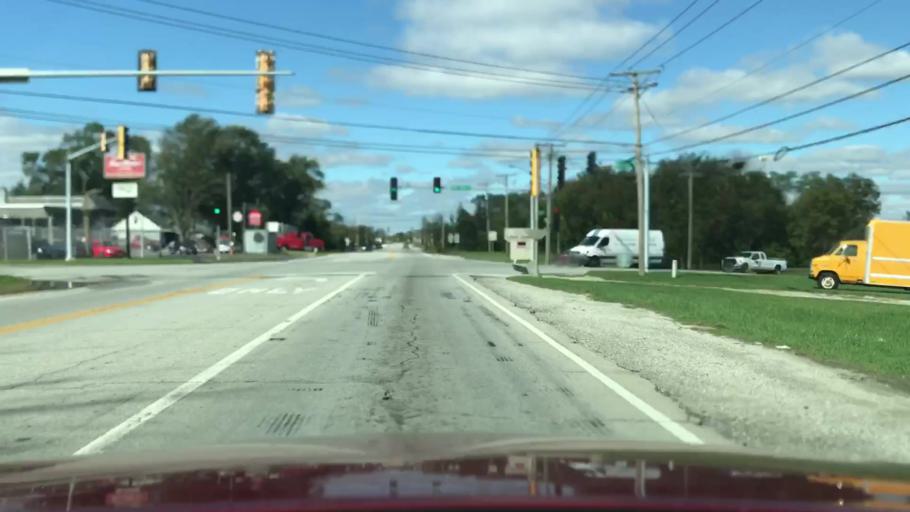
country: US
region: Illinois
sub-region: Cook County
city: Glenwood
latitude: 41.5314
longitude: -87.5774
